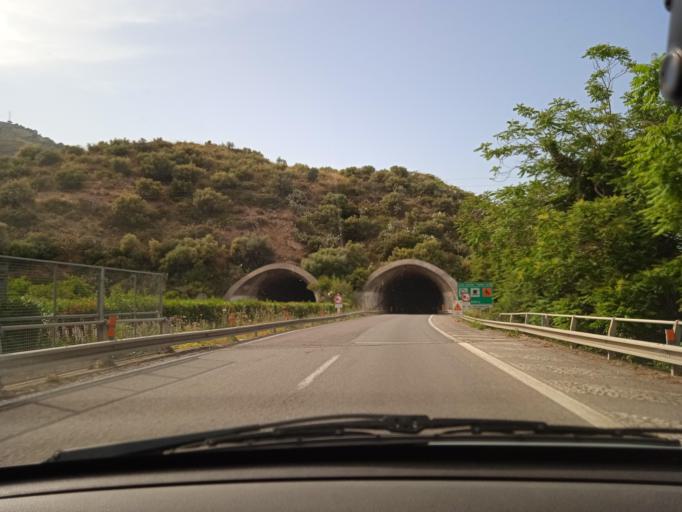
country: IT
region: Sicily
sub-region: Messina
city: Oliveri
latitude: 38.1220
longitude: 15.0555
